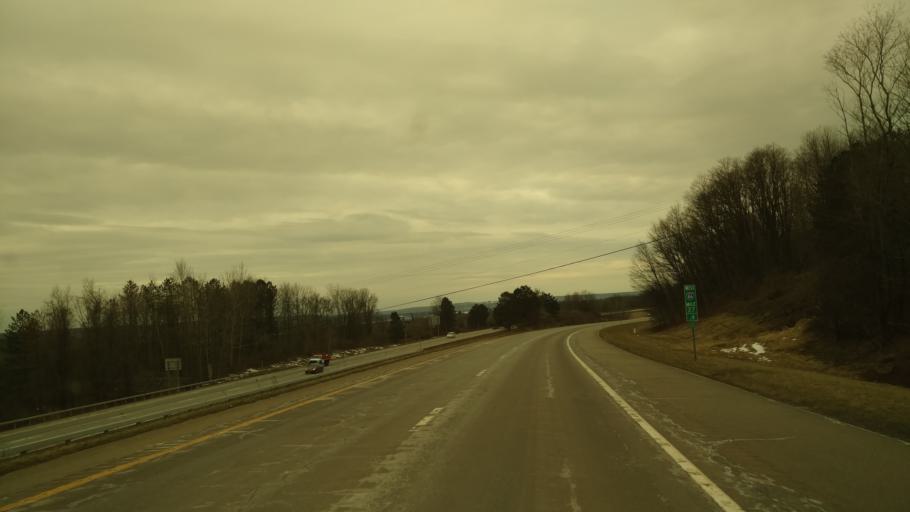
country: US
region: New York
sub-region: Chautauqua County
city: Jamestown
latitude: 42.1204
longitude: -79.2530
